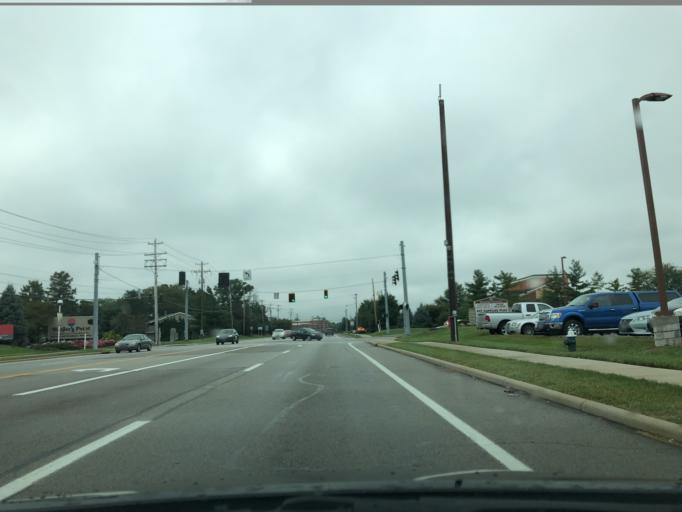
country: US
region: Ohio
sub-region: Hamilton County
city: Sixteen Mile Stand
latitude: 39.2709
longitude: -84.3287
